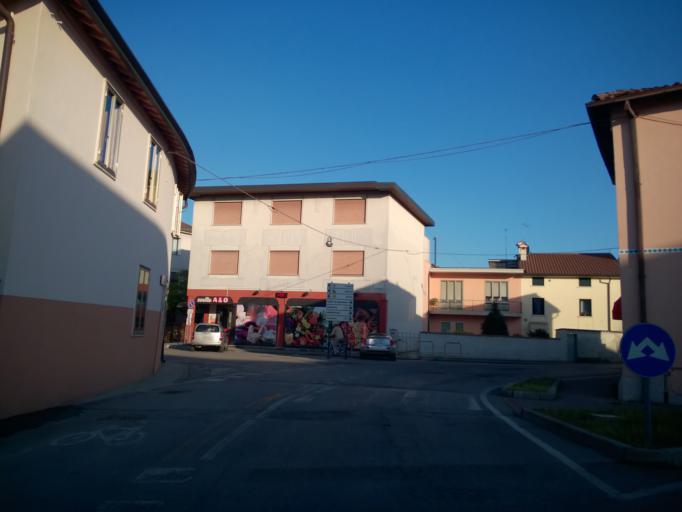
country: IT
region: Veneto
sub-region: Provincia di Vicenza
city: Marano Vicentino
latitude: 45.6921
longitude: 11.4282
